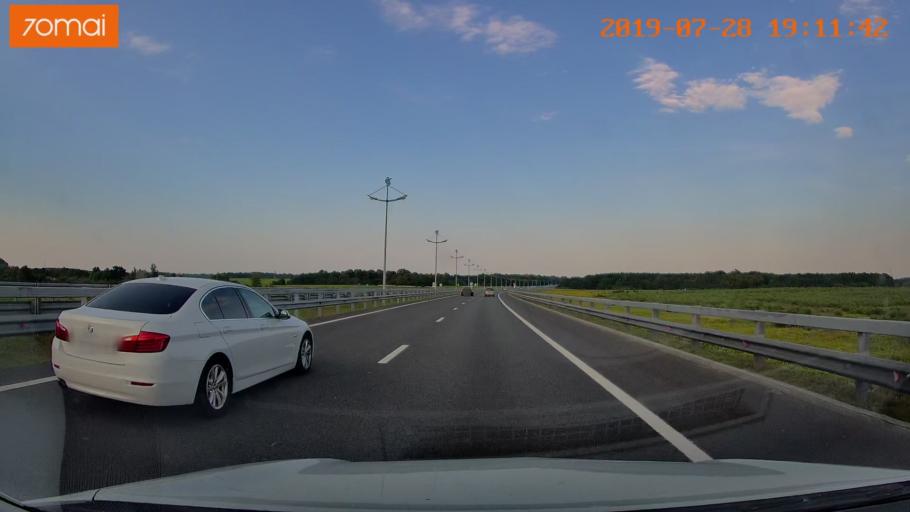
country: RU
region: Kaliningrad
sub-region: Gorod Kaliningrad
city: Pionerskiy
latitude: 54.9163
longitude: 20.2363
